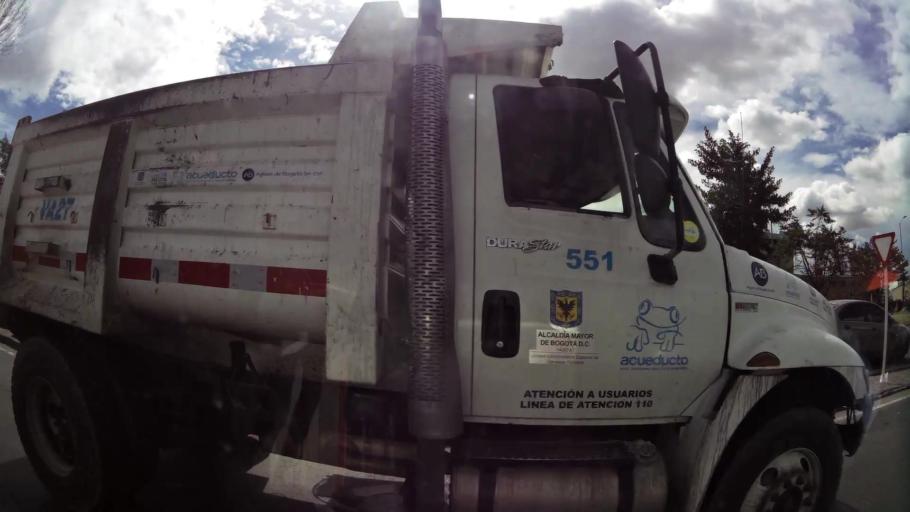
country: CO
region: Bogota D.C.
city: Bogota
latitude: 4.6245
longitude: -74.1382
